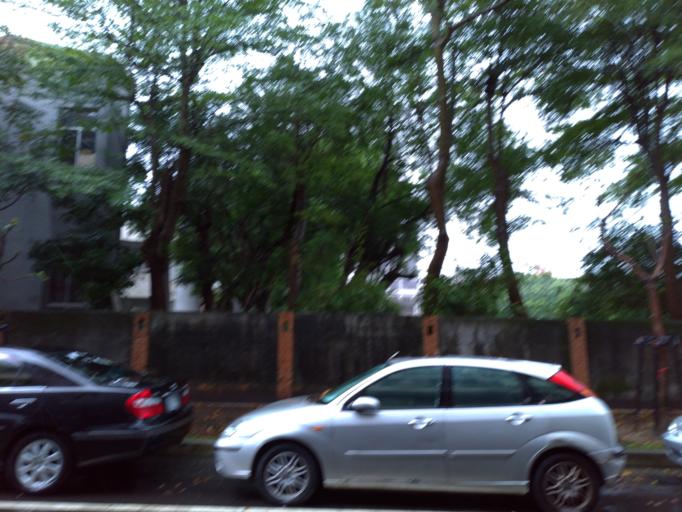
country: TW
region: Taiwan
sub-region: Keelung
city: Keelung
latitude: 25.0829
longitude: 121.6978
